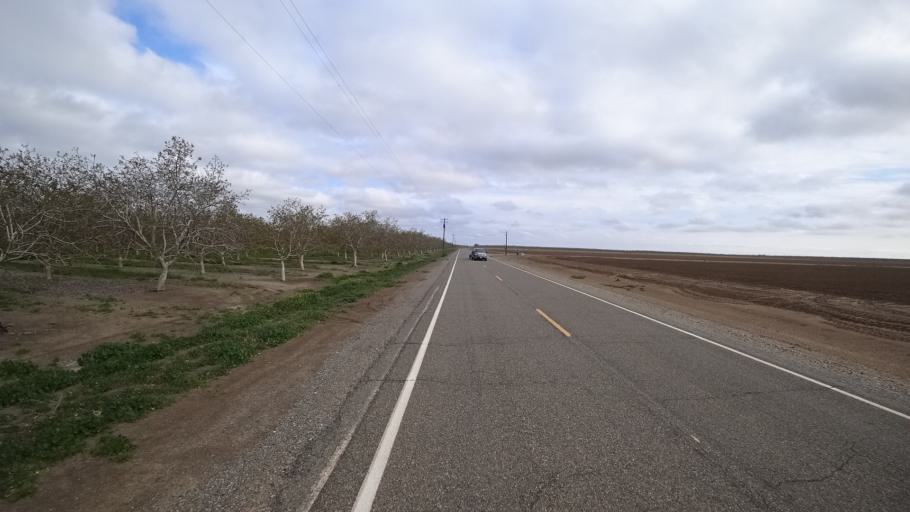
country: US
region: California
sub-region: Colusa County
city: Colusa
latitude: 39.4452
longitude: -121.9677
